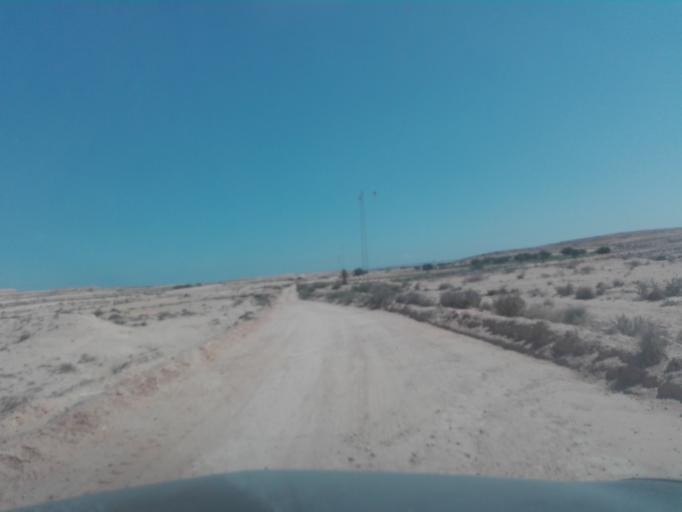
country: TN
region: Qabis
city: Gabes
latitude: 33.8442
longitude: 9.9839
